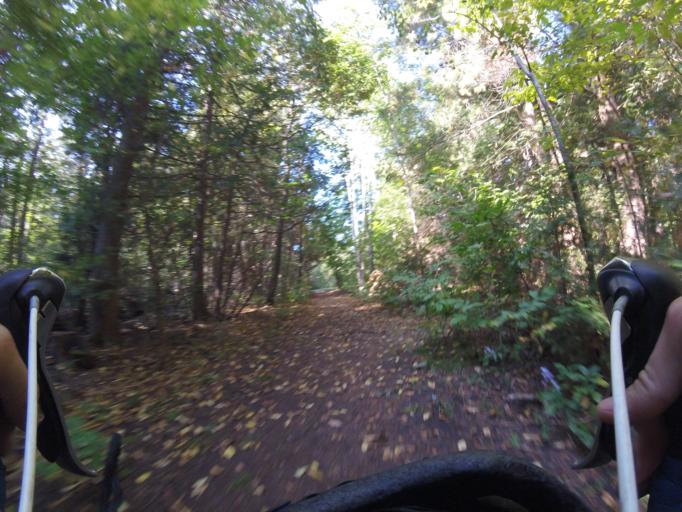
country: CA
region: Ontario
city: Bells Corners
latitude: 45.3050
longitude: -75.8923
